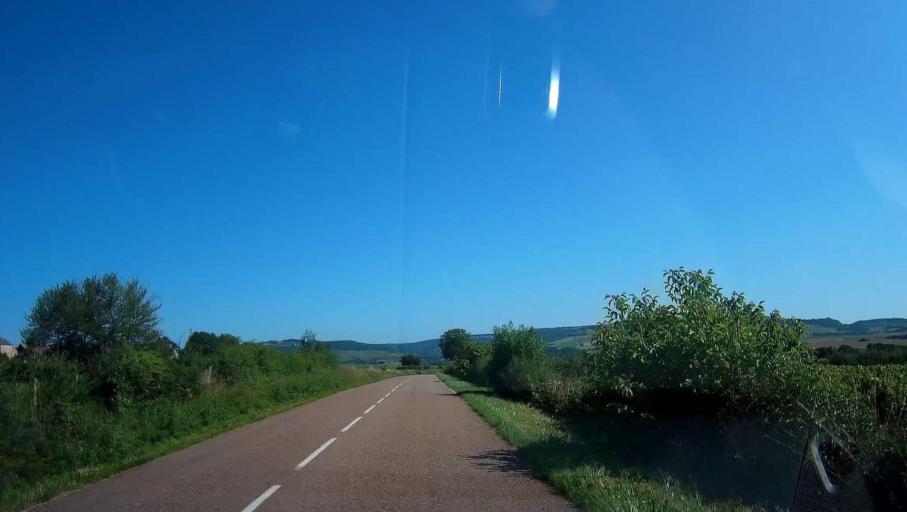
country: FR
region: Bourgogne
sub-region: Departement de la Cote-d'Or
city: Nolay
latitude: 46.9262
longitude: 4.6230
